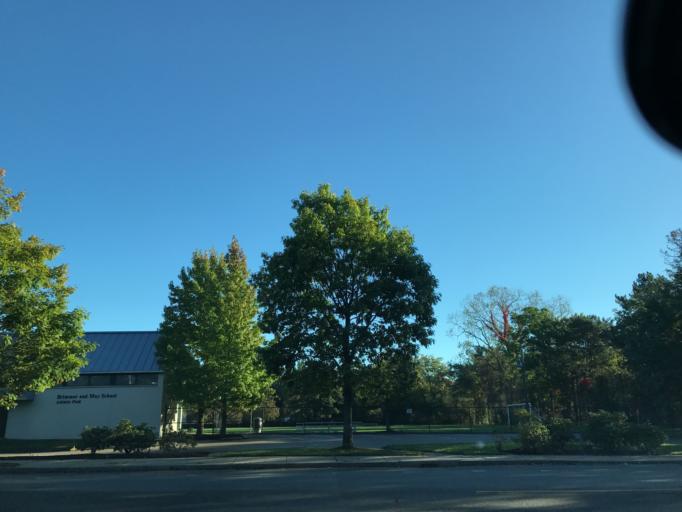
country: US
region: Massachusetts
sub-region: Middlesex County
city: Newton
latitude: 42.2947
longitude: -71.1790
